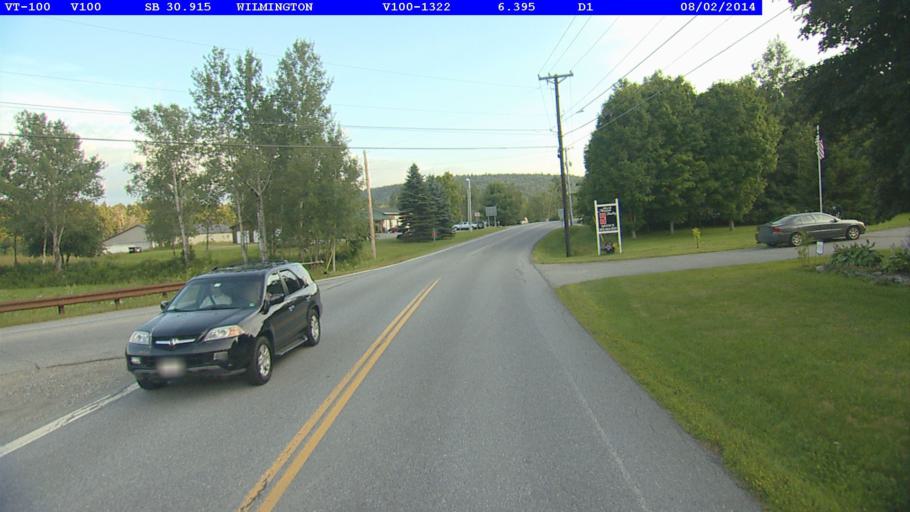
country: US
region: Vermont
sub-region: Windham County
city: Dover
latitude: 42.9134
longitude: -72.8393
